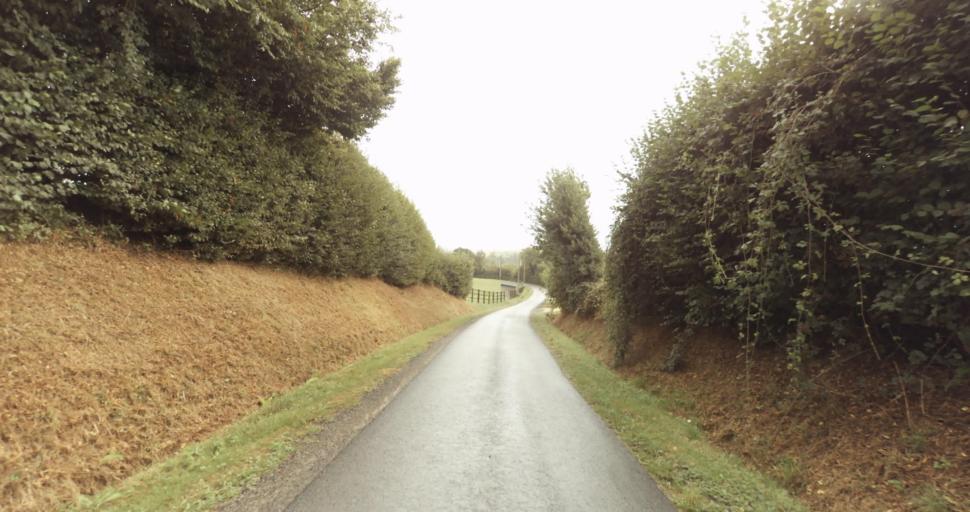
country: FR
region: Lower Normandy
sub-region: Departement de l'Orne
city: Sainte-Gauburge-Sainte-Colombe
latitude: 48.6954
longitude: 0.4095
